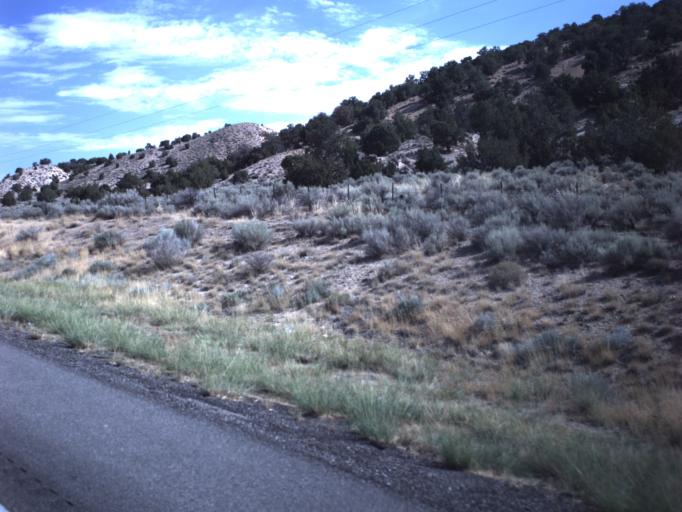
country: US
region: Utah
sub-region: Sanpete County
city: Gunnison
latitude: 39.3535
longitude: -111.9295
